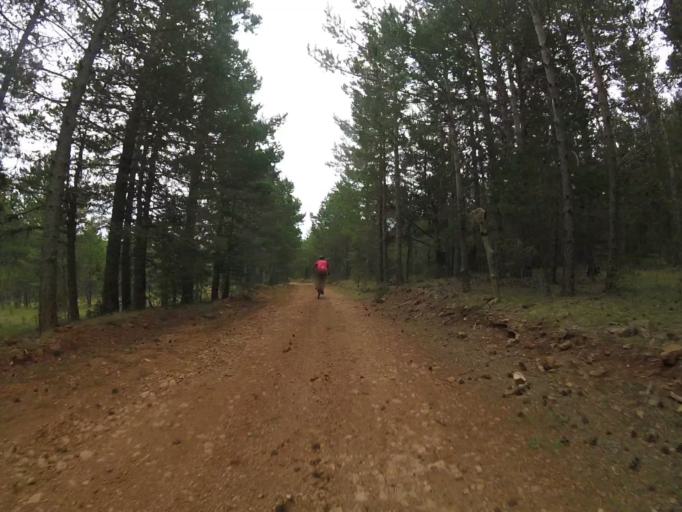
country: ES
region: Aragon
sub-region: Provincia de Teruel
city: Valdelinares
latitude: 40.3611
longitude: -0.6146
